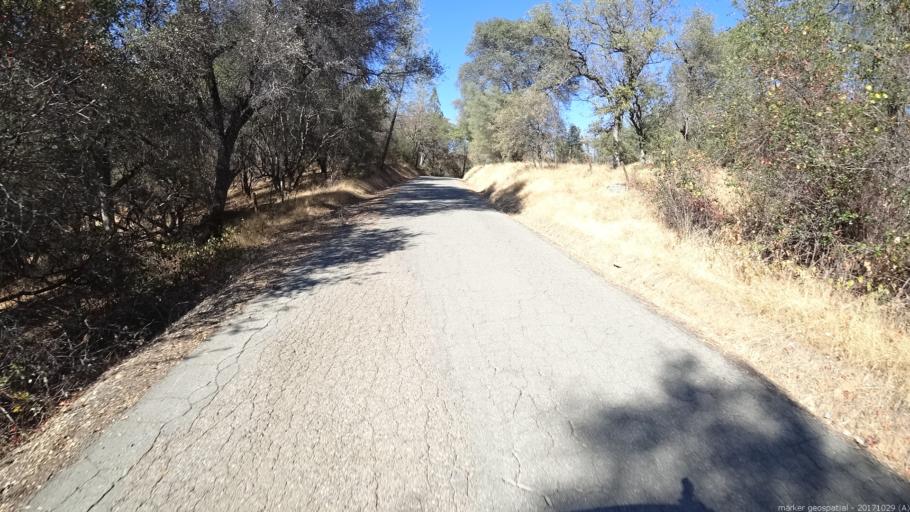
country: US
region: California
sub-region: Shasta County
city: Shasta
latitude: 40.4839
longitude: -122.6754
